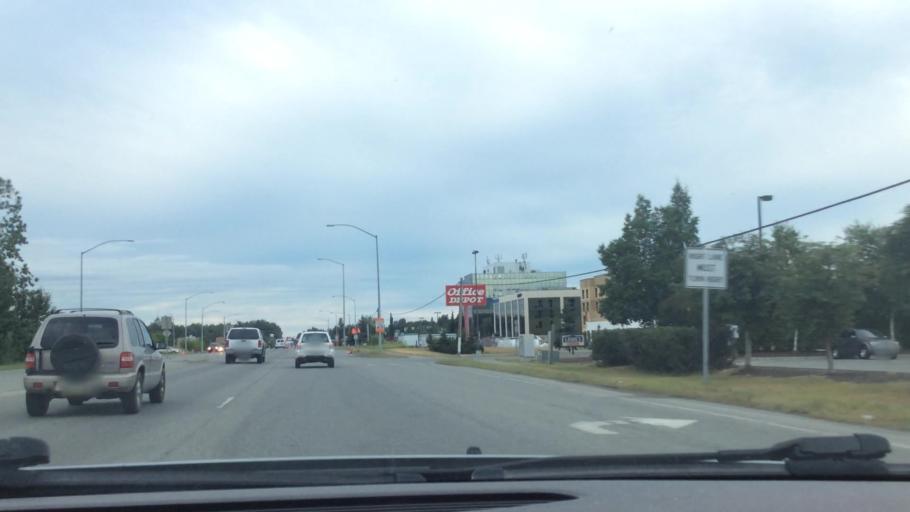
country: US
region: Alaska
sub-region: Anchorage Municipality
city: Anchorage
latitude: 61.1809
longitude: -149.8791
